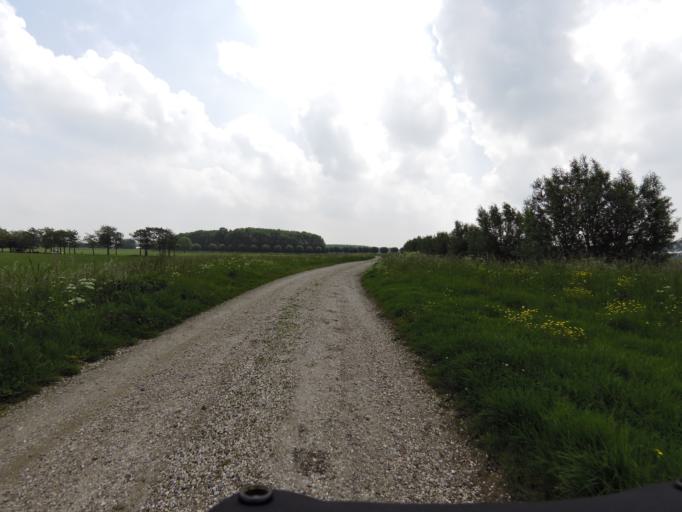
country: NL
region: South Holland
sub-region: Gemeente Spijkenisse
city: Spijkenisse
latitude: 51.8400
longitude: 4.2564
